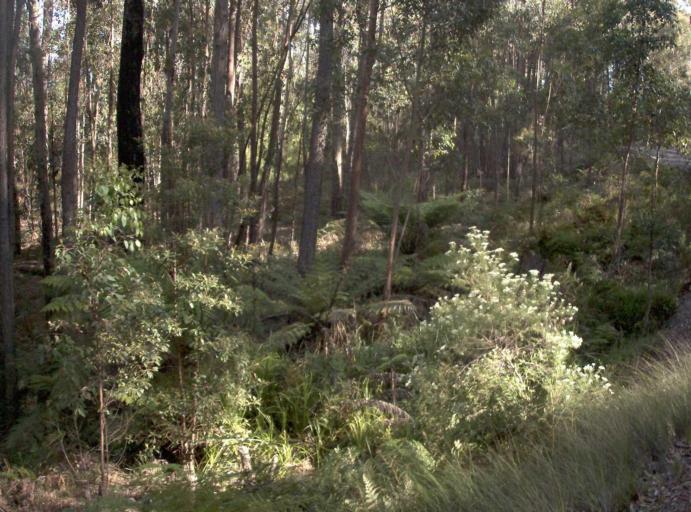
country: AU
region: Victoria
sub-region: East Gippsland
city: Lakes Entrance
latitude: -37.6316
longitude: 148.4874
